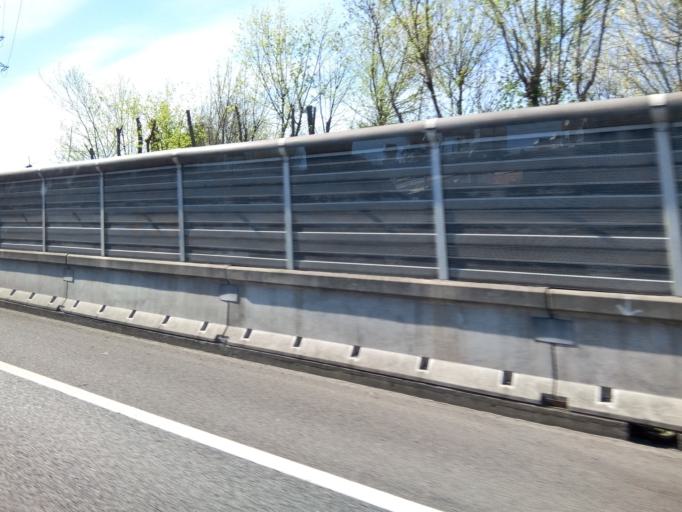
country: IT
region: Lombardy
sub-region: Citta metropolitana di Milano
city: Arese
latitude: 45.5426
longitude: 9.0705
